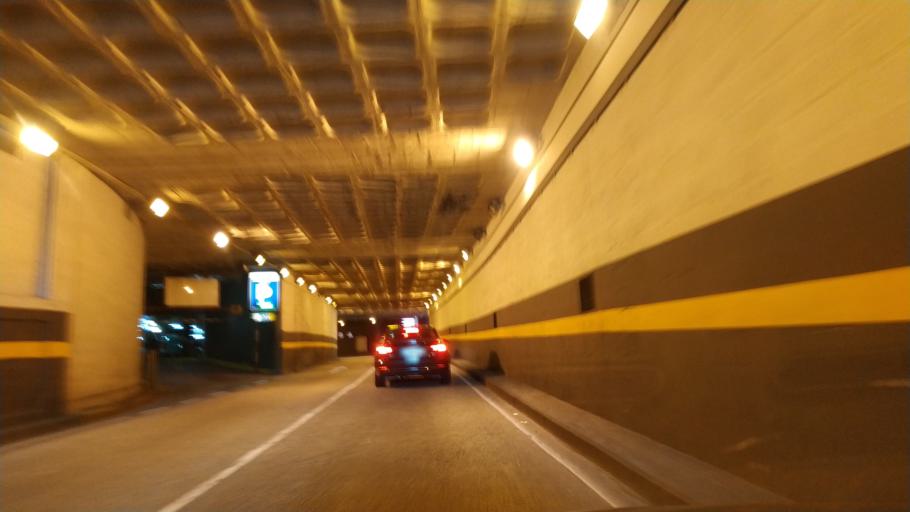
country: ES
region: Galicia
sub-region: Provincia da Coruna
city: A Coruna
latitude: 43.3679
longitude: -8.4065
